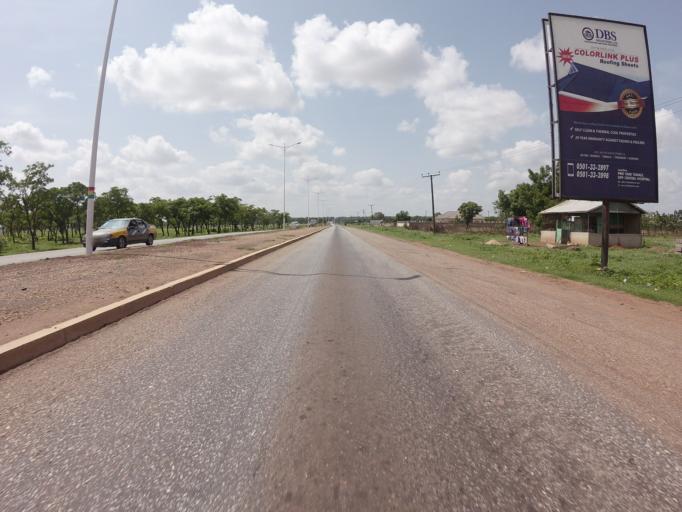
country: GH
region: Northern
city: Savelugu
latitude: 9.5537
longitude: -0.8372
